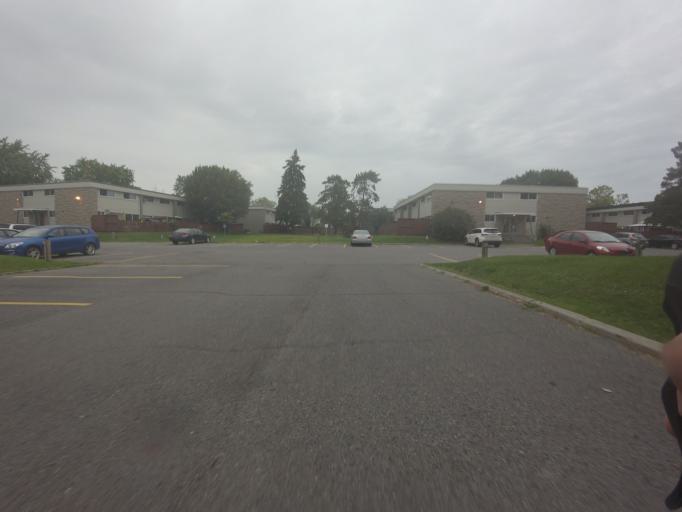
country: CA
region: Ontario
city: Ottawa
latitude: 45.3619
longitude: -75.7164
